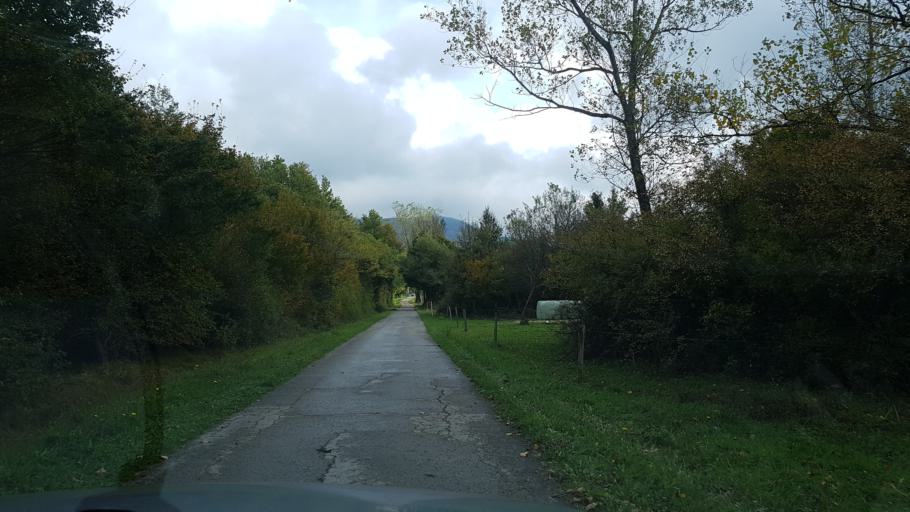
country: HR
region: Istarska
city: Buzet
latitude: 45.4126
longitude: 14.0984
